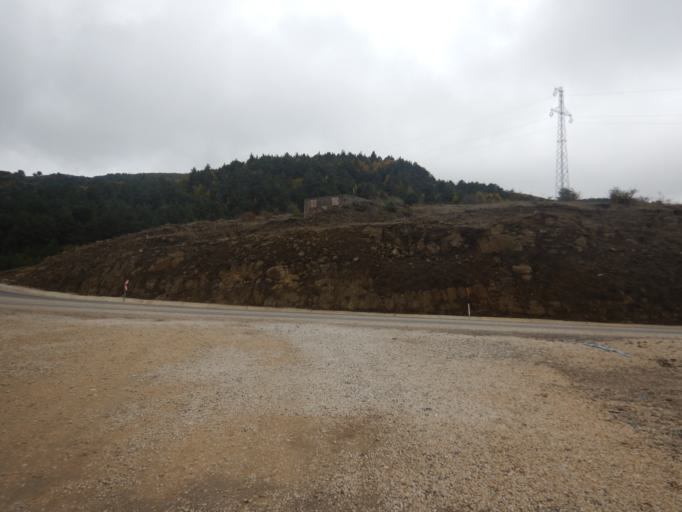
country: TR
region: Ordu
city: Mesudiye
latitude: 40.4331
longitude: 37.7769
